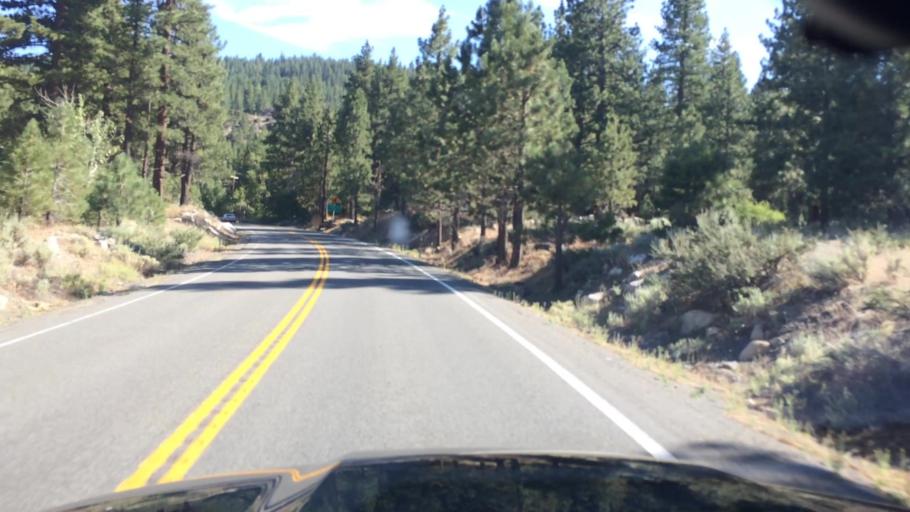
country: US
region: Nevada
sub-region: Washoe County
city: Incline Village
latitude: 39.3569
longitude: -119.8562
